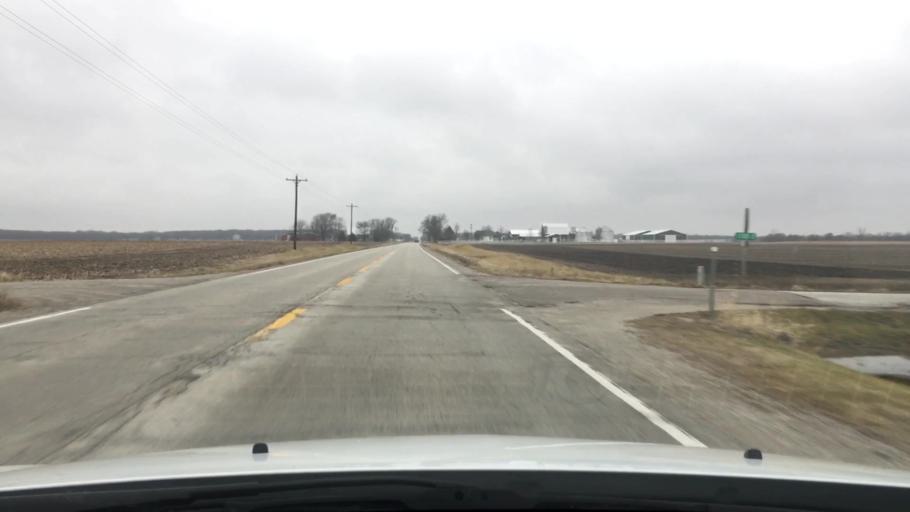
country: US
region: Illinois
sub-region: Iroquois County
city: Watseka
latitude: 40.8883
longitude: -87.8079
